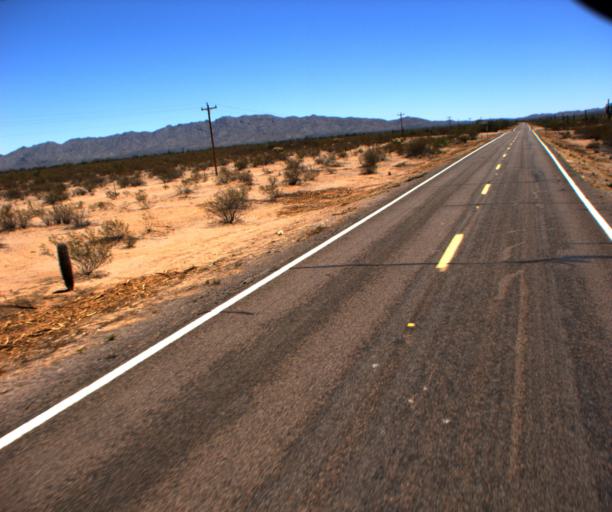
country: US
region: Arizona
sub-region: Pima County
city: Sells
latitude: 32.1816
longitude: -112.3302
